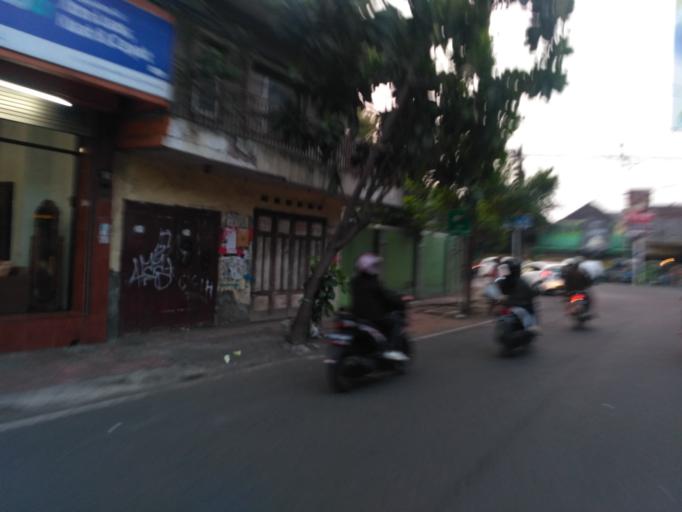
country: ID
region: East Java
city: Malang
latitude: -7.9812
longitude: 112.6275
